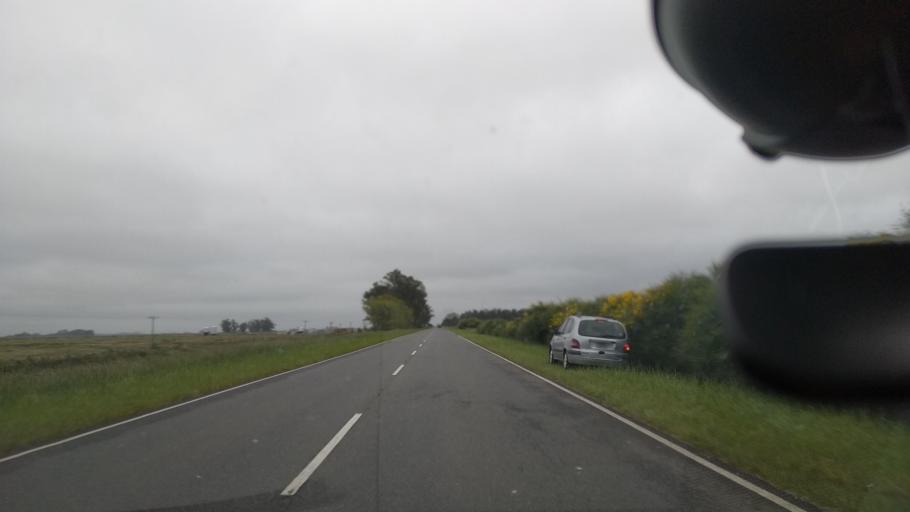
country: AR
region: Buenos Aires
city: Veronica
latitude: -35.4602
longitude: -57.3291
